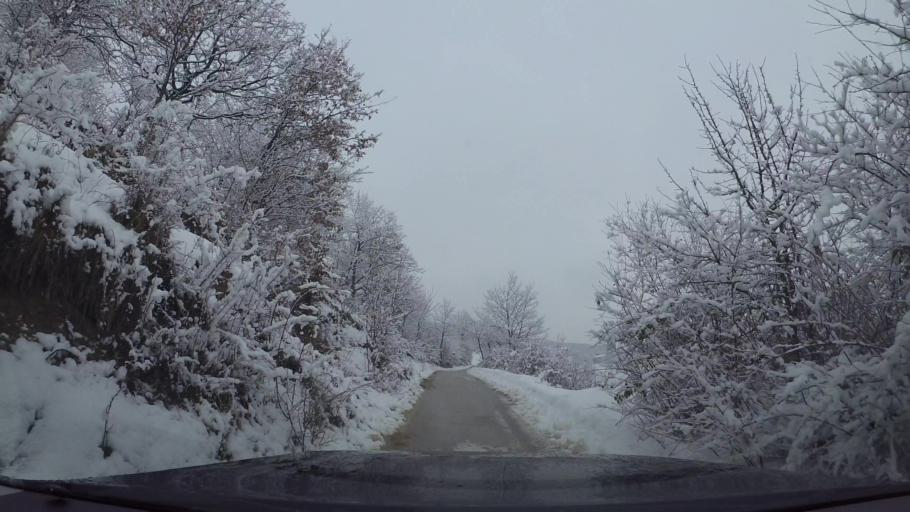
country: BA
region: Federation of Bosnia and Herzegovina
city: Vogosca
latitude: 43.8772
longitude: 18.3233
